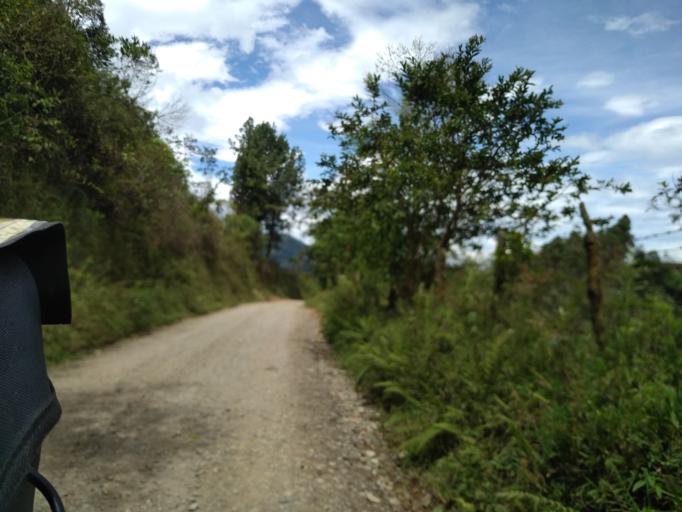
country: CO
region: Quindio
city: Salento
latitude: 4.6279
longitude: -75.5853
